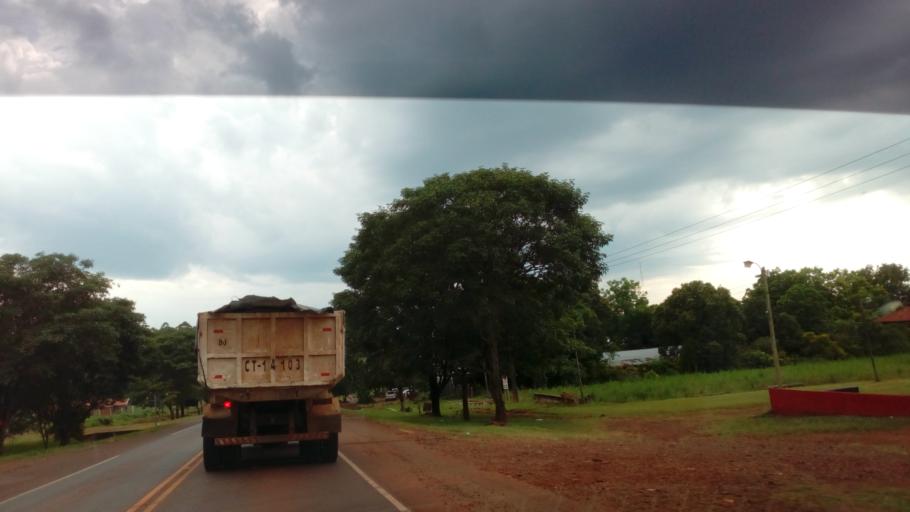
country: PY
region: Itapua
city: Obligado
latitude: -27.0716
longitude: -55.6148
